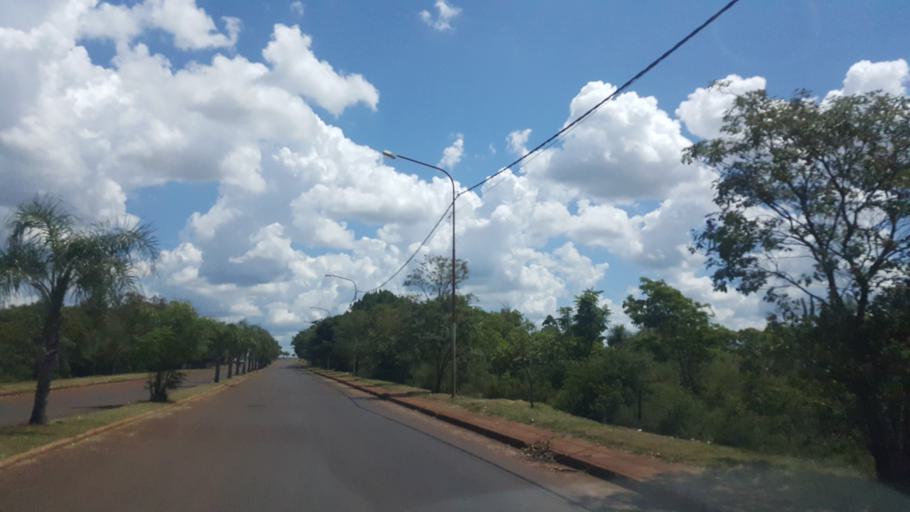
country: AR
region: Misiones
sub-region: Departamento de Capital
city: Posadas
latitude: -27.3740
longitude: -55.9611
